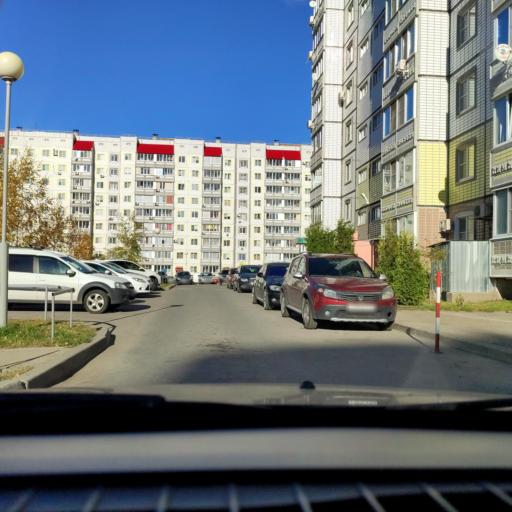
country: RU
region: Samara
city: Tol'yatti
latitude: 53.5241
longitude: 49.3347
